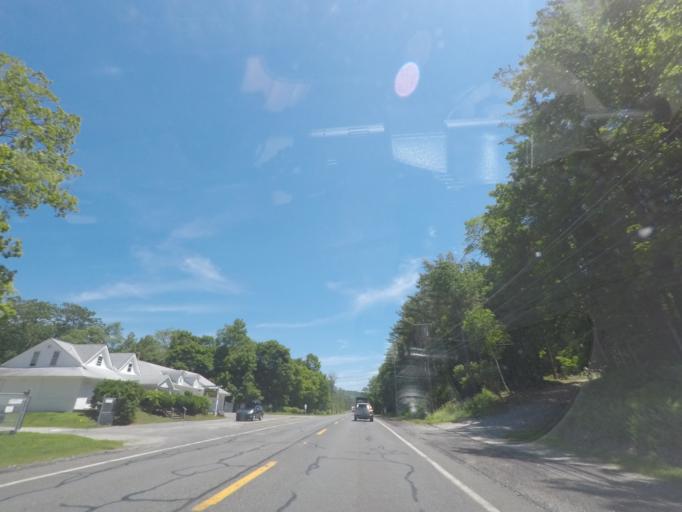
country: US
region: Massachusetts
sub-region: Berkshire County
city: Lee
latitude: 42.2972
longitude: -73.1906
